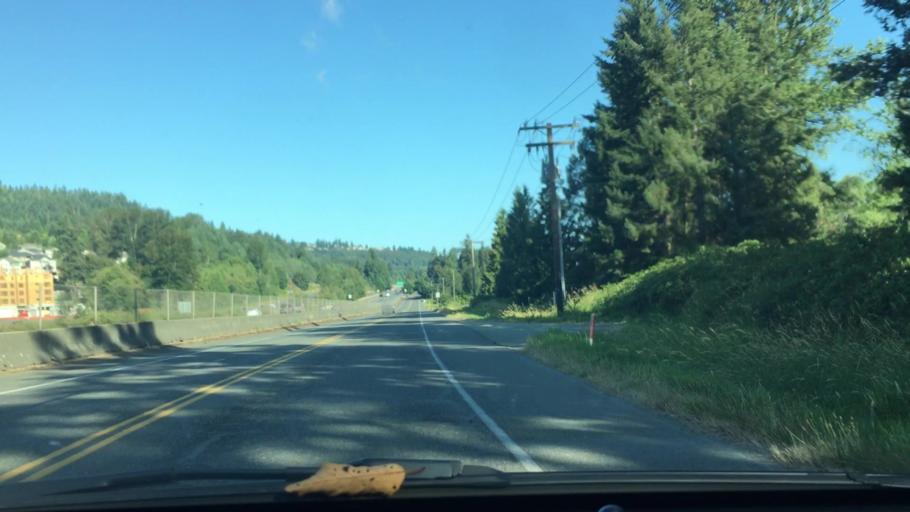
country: US
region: Washington
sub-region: King County
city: West Lake Sammamish
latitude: 47.5539
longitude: -122.0697
